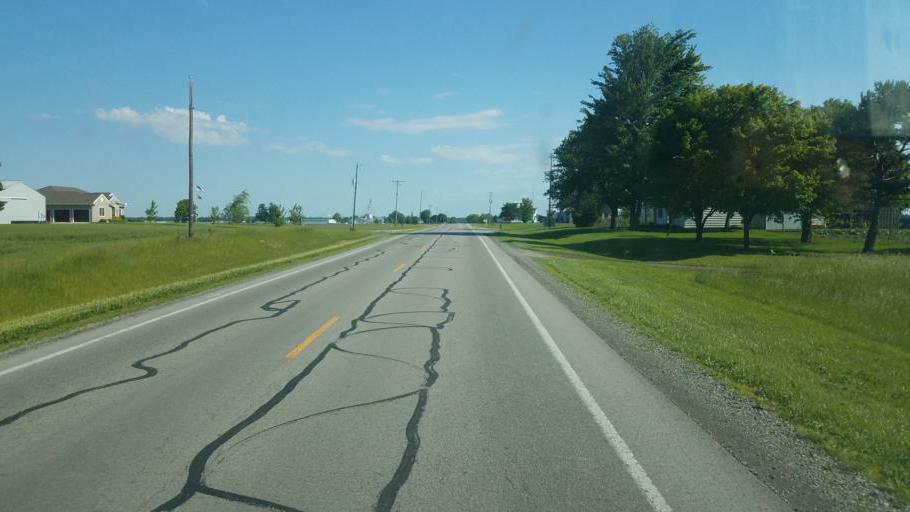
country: US
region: Ohio
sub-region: Hardin County
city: Kenton
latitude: 40.6070
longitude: -83.5951
